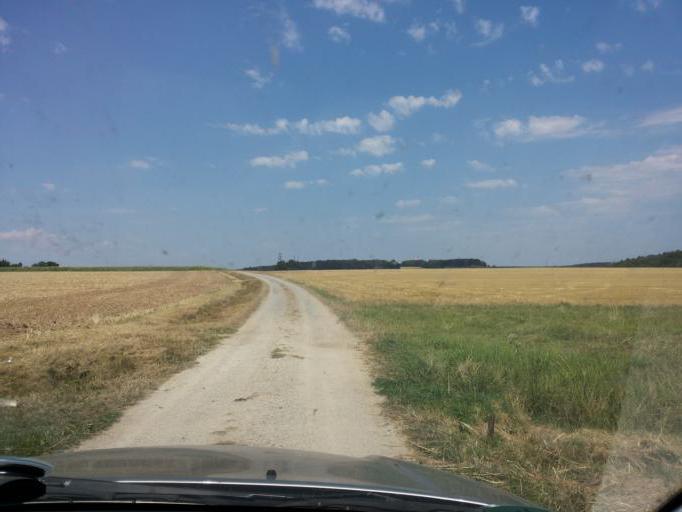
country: DE
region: Bavaria
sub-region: Regierungsbezirk Mittelfranken
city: Hagenbuchach
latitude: 49.5174
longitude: 10.7518
